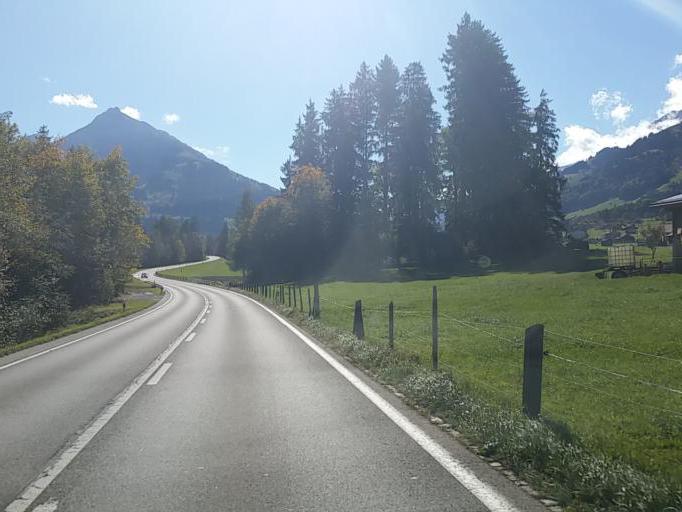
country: CH
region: Bern
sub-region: Frutigen-Niedersimmental District
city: Frutigen
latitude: 46.6017
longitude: 7.6615
